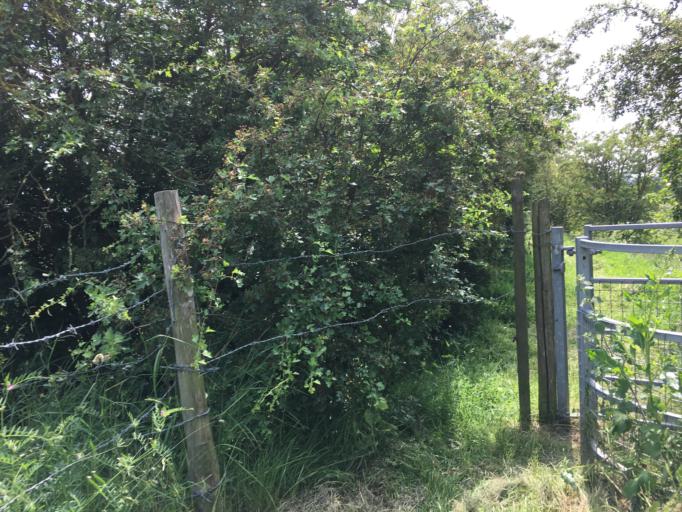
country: GB
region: England
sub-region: Kent
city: Queenborough
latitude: 51.3827
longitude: 0.7535
